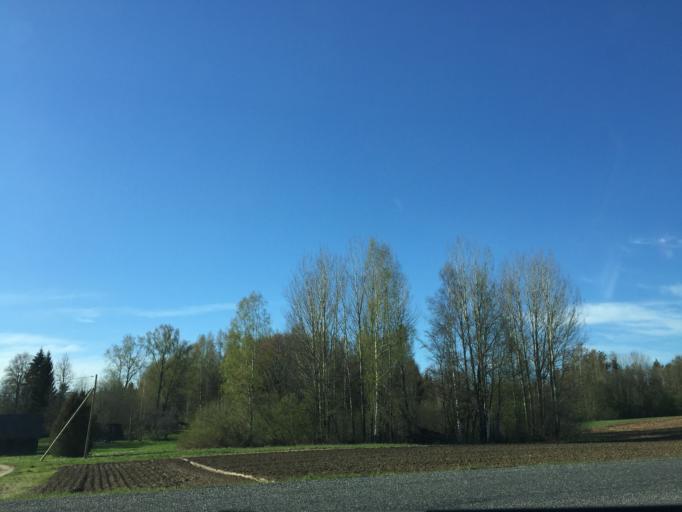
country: EE
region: Valgamaa
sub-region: Valga linn
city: Valga
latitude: 57.8385
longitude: 26.2358
